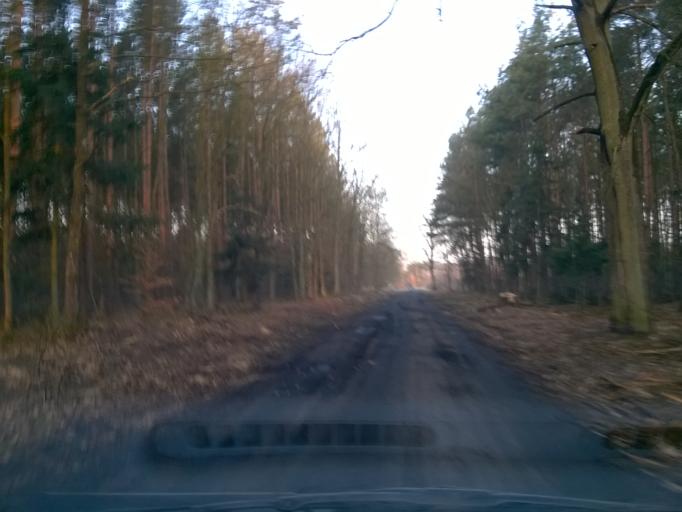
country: PL
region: Kujawsko-Pomorskie
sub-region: Powiat nakielski
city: Sadki
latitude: 53.1219
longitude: 17.4263
